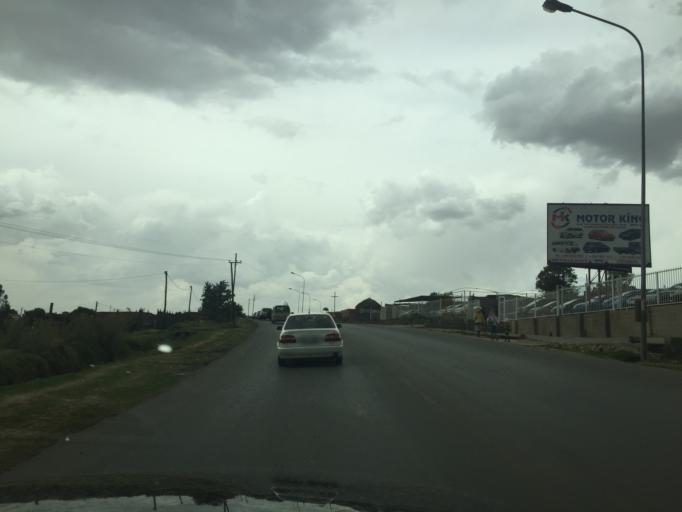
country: LS
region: Maseru
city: Maseru
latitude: -29.2973
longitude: 27.5178
